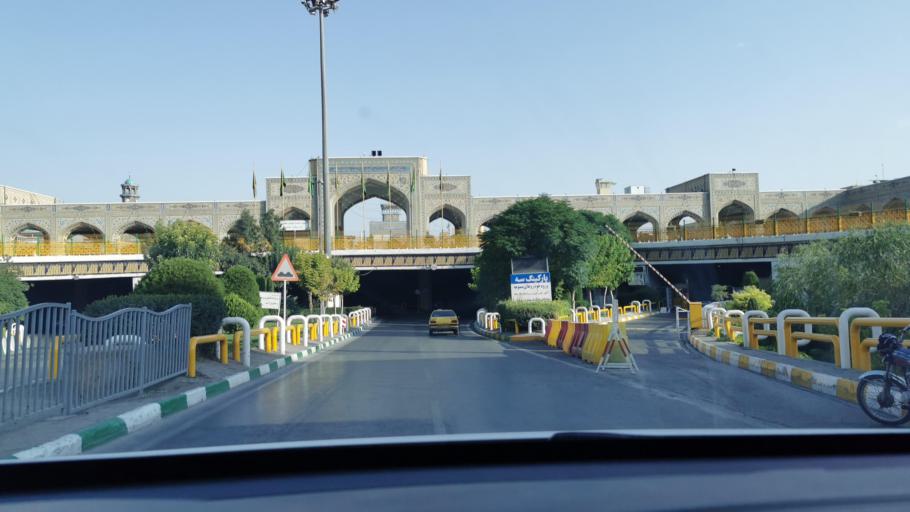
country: IR
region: Razavi Khorasan
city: Mashhad
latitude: 36.2860
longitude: 59.6187
